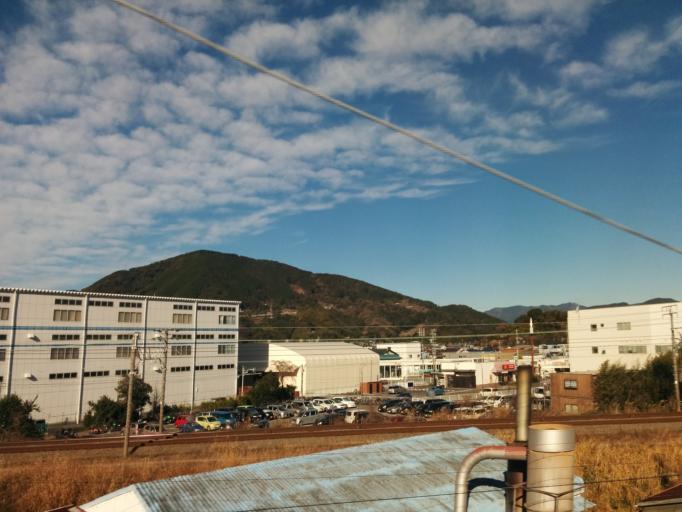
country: JP
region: Shizuoka
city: Shizuoka-shi
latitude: 34.9510
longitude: 138.3664
